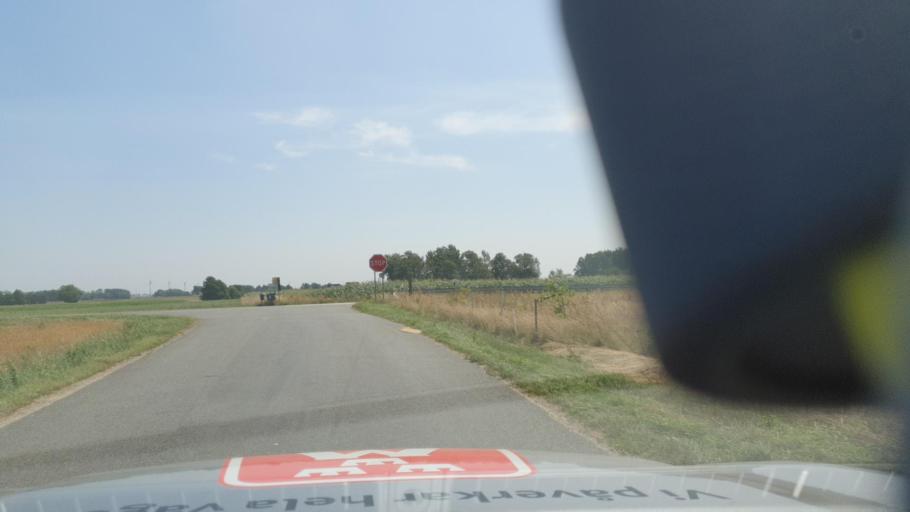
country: SE
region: Skane
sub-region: Tomelilla Kommun
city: Tomelilla
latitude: 55.5508
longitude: 14.0651
